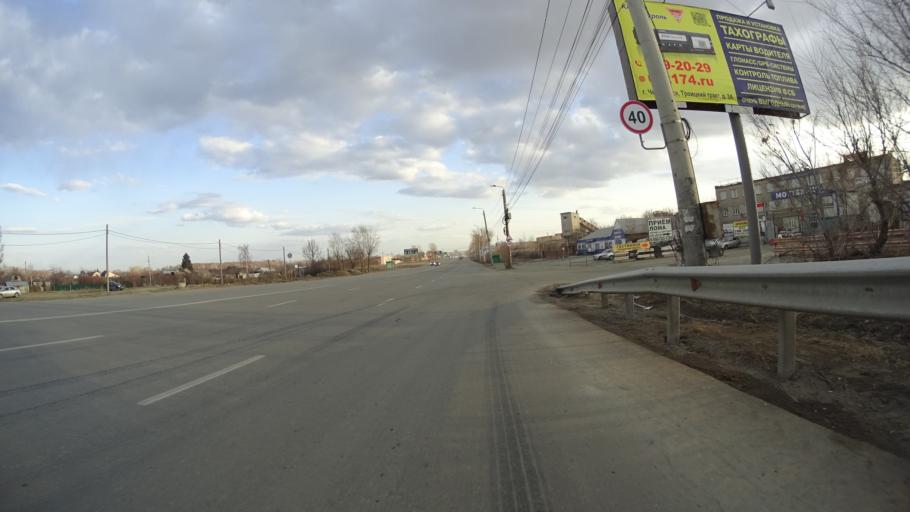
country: RU
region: Chelyabinsk
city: Novosineglazovskiy
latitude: 55.0991
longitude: 61.3876
